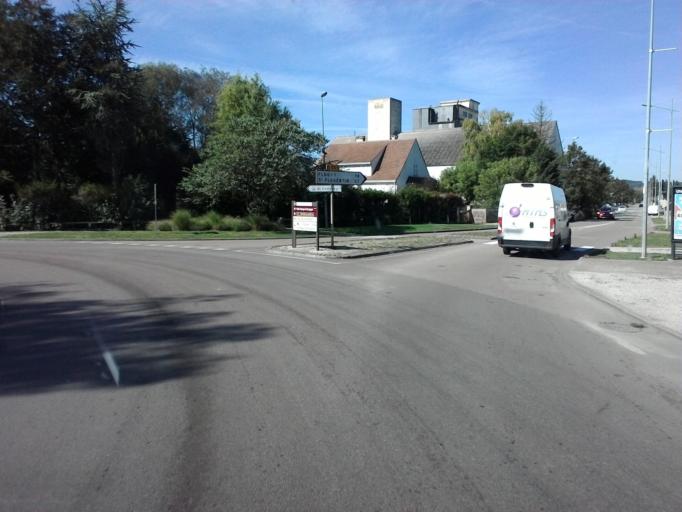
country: FR
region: Bourgogne
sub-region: Departement de l'Yonne
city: Tonnerre
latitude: 47.8635
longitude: 3.9825
